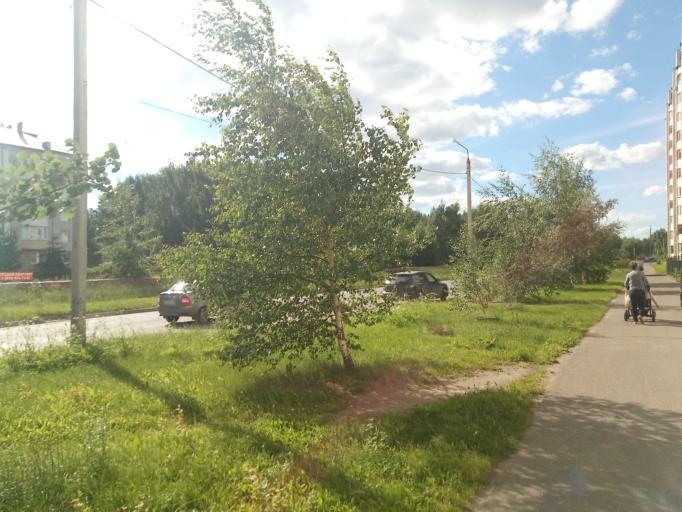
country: RU
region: Jaroslavl
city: Yaroslavl
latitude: 57.6400
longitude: 39.9475
